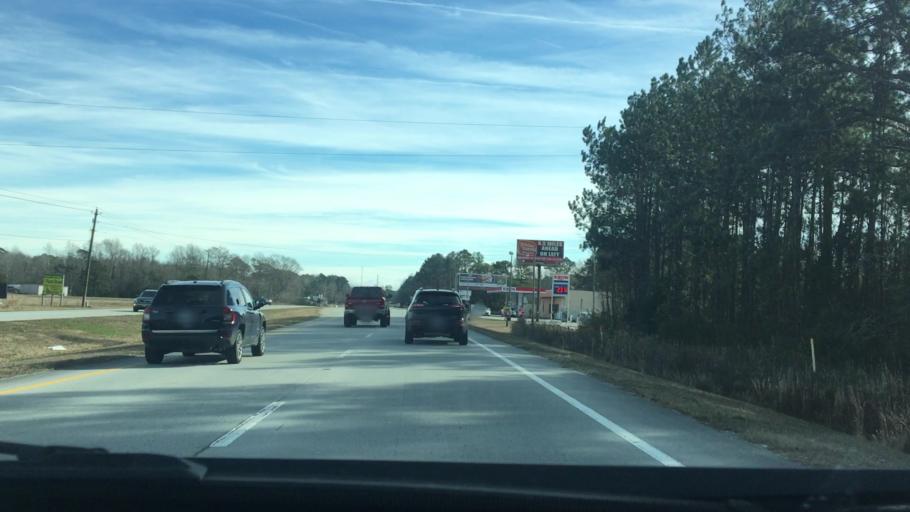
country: US
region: North Carolina
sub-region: Carteret County
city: Newport
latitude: 34.7508
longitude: -76.8407
